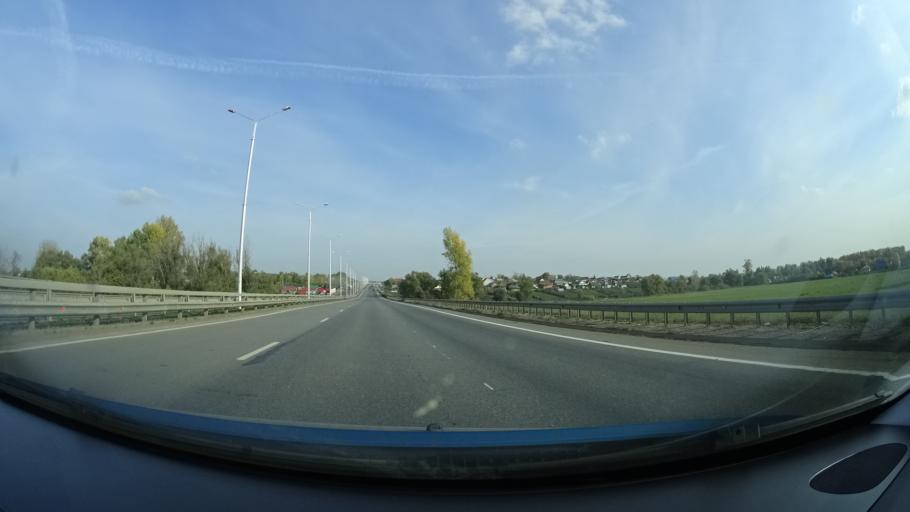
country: RU
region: Bashkortostan
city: Avdon
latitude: 54.6455
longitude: 55.5488
